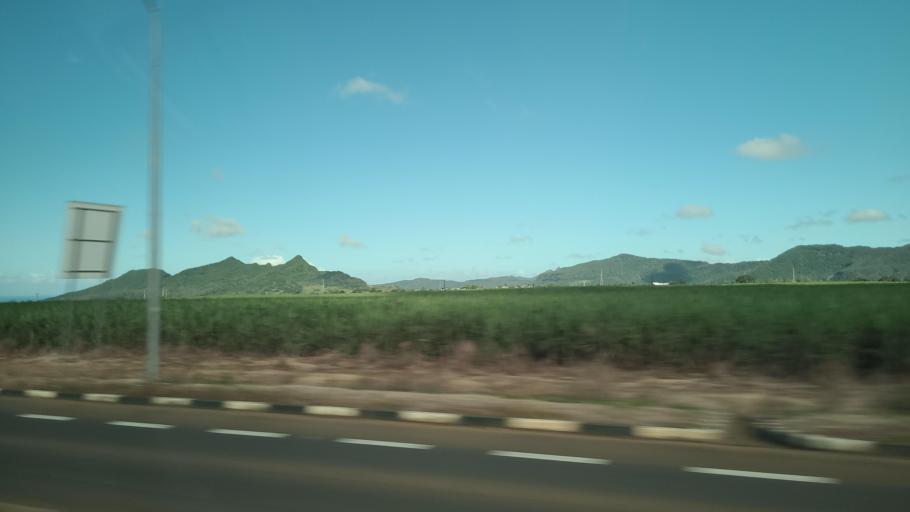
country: MU
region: Flacq
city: Camp de Masque
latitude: -20.2310
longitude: 57.6583
